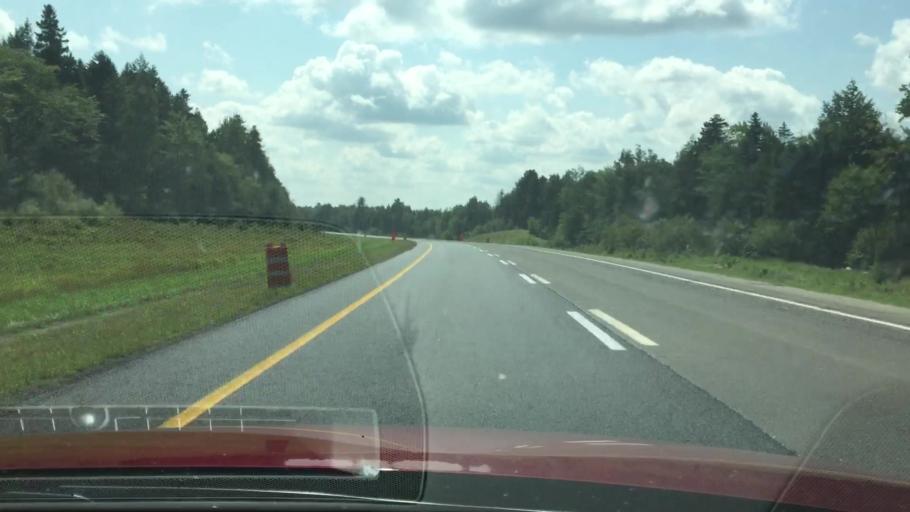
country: US
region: Maine
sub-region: Penobscot County
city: Medway
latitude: 45.7011
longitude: -68.4850
